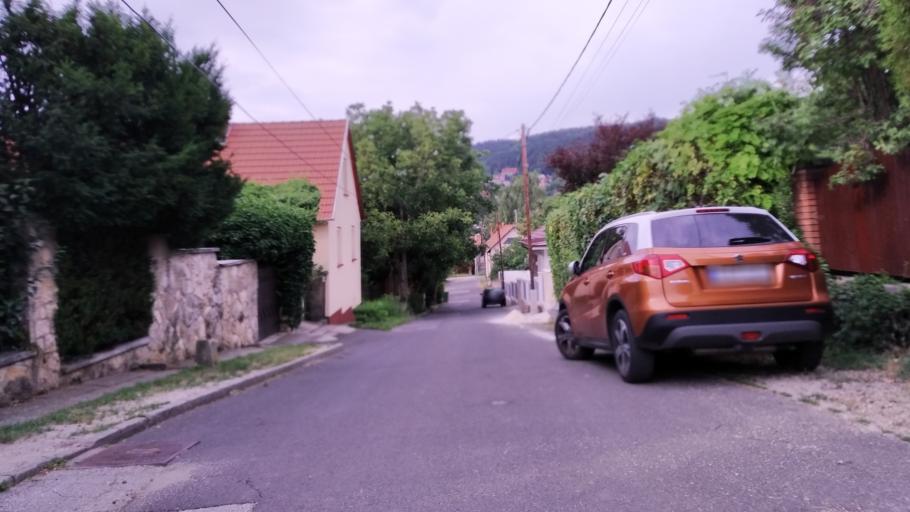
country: HU
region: Pest
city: Budakalasz
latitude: 47.6002
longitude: 19.0434
